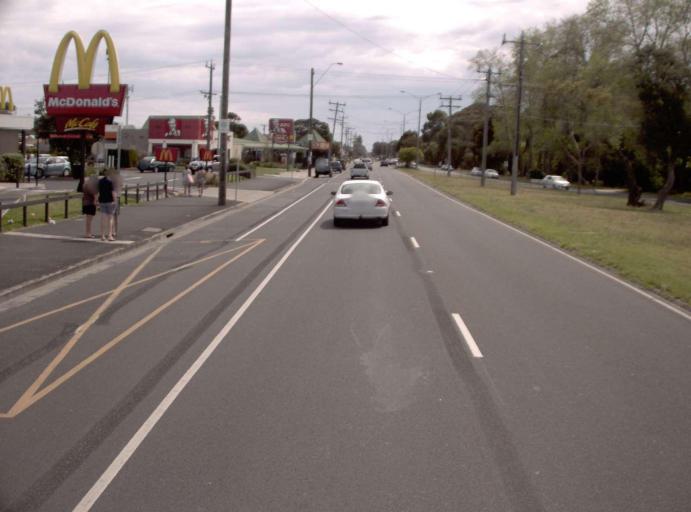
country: AU
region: Victoria
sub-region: Mornington Peninsula
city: Rosebud
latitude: -38.3575
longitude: 144.8988
